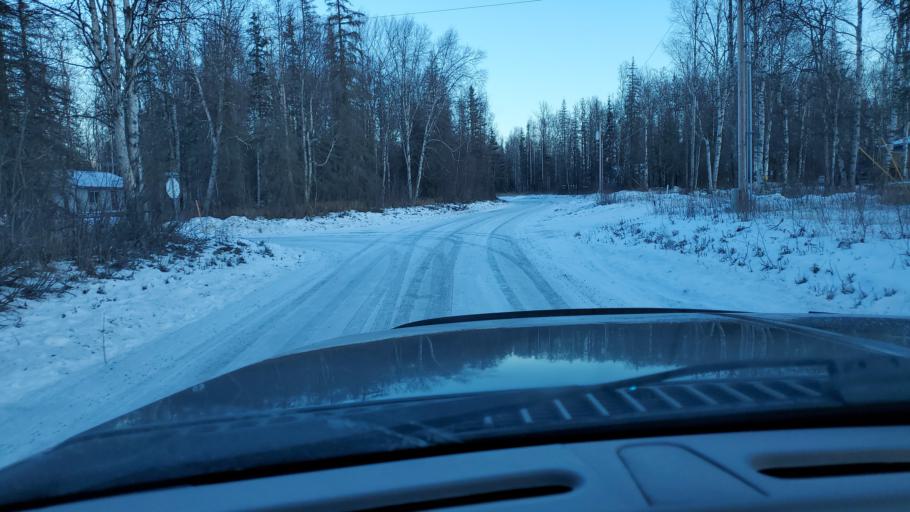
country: US
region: Alaska
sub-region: Matanuska-Susitna Borough
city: Lakes
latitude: 61.6653
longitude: -149.2980
